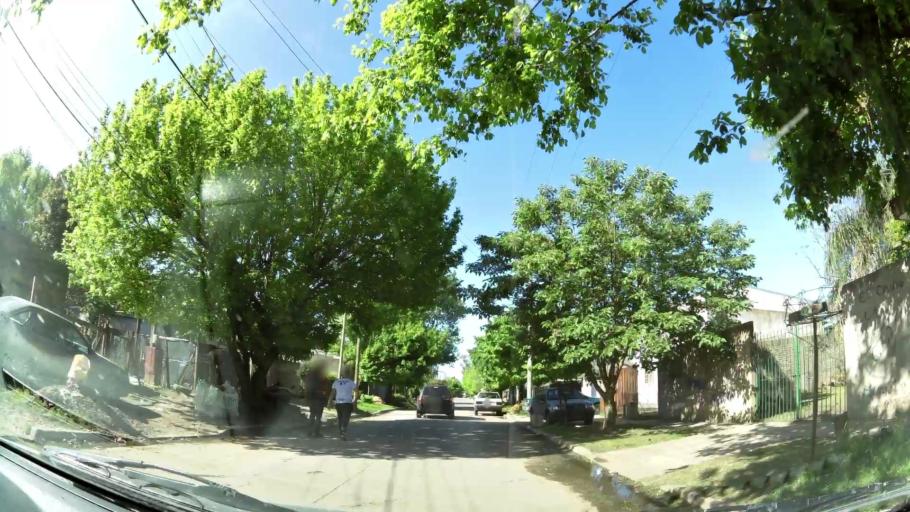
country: AR
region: Buenos Aires
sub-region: Partido de Quilmes
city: Quilmes
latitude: -34.8007
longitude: -58.2339
